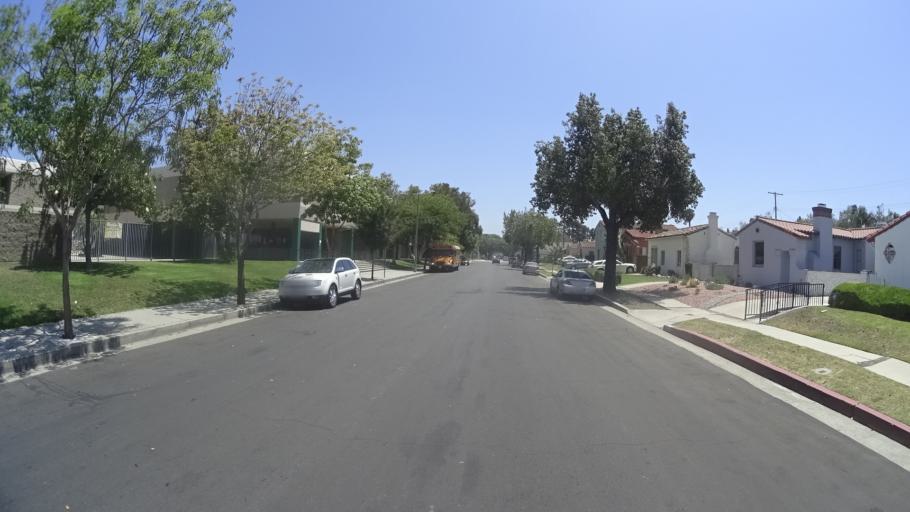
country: US
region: California
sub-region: Los Angeles County
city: View Park-Windsor Hills
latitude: 34.0099
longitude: -118.3296
